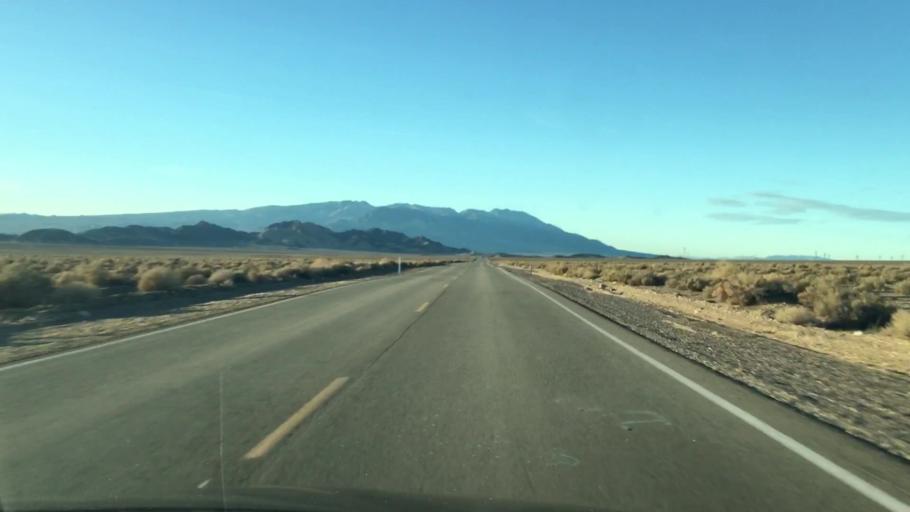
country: US
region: California
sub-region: San Bernardino County
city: Fort Irwin
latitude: 35.3555
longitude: -116.0967
